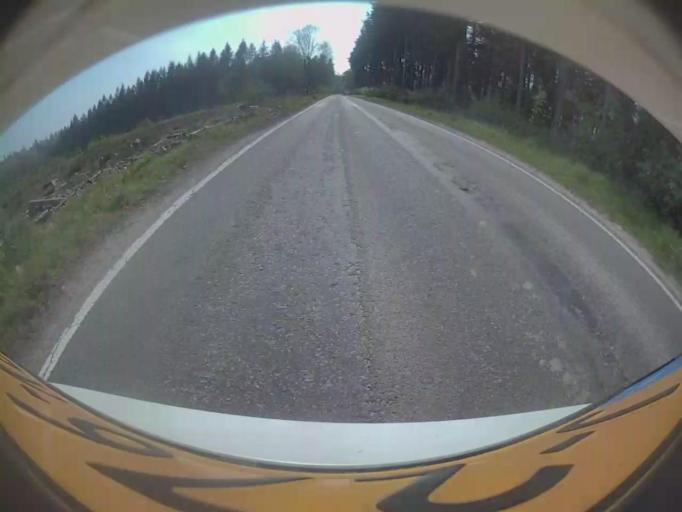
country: BE
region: Wallonia
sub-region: Province de Namur
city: Hamois
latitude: 50.2906
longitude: 5.1993
